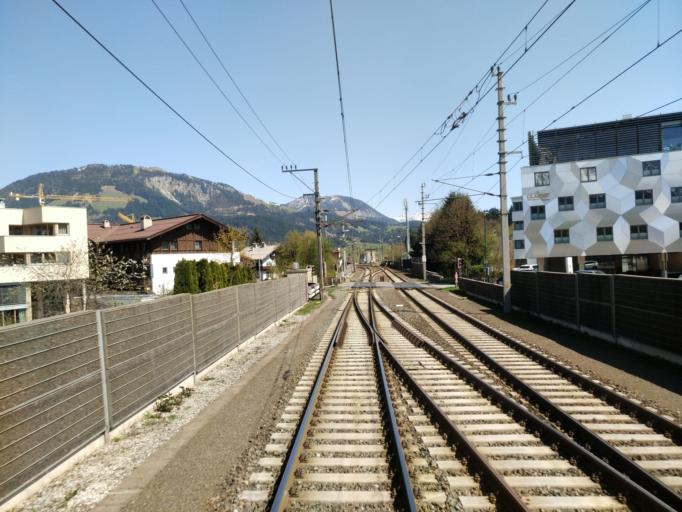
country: AT
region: Tyrol
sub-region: Politischer Bezirk Kitzbuhel
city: Sankt Johann in Tirol
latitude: 47.5198
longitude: 12.4241
